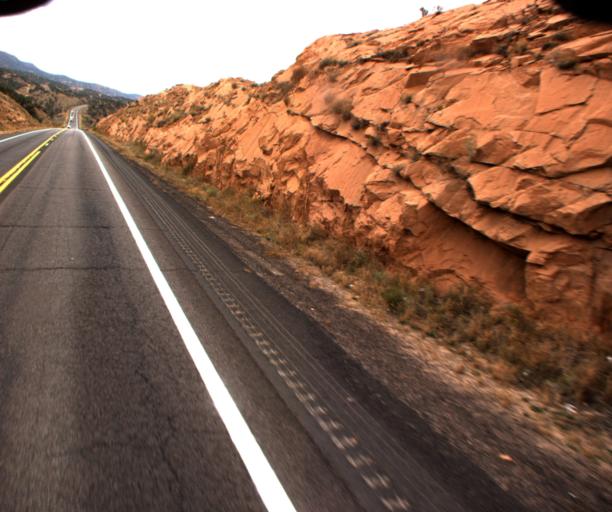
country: US
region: Arizona
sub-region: Navajo County
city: Kayenta
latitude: 36.6604
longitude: -110.4197
